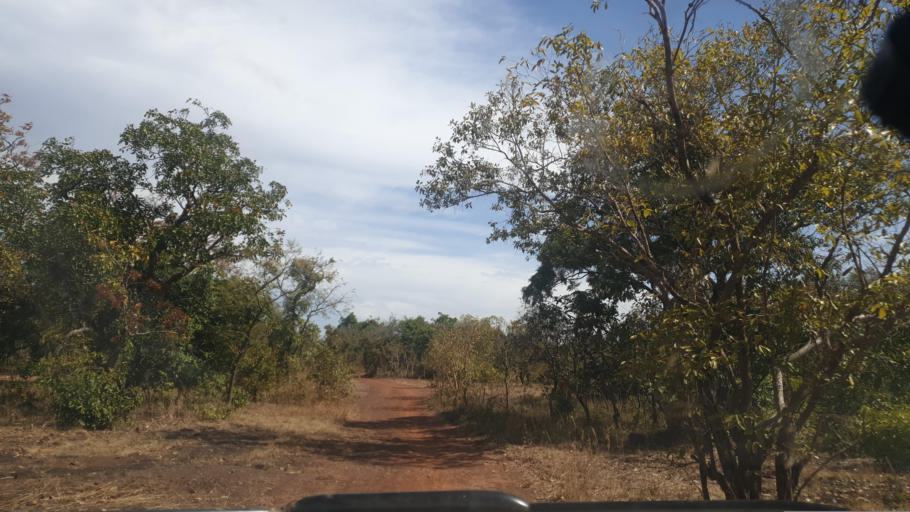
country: ML
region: Sikasso
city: Yanfolila
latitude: 10.4969
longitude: -7.9610
